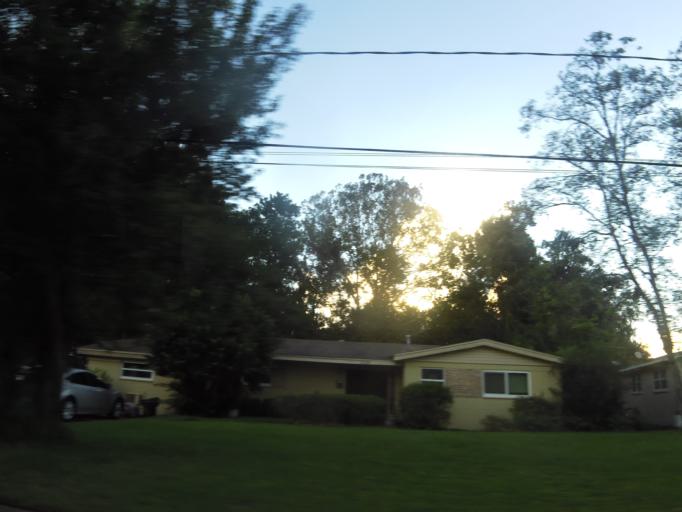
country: US
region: Florida
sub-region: Duval County
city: Jacksonville
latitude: 30.2327
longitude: -81.6136
